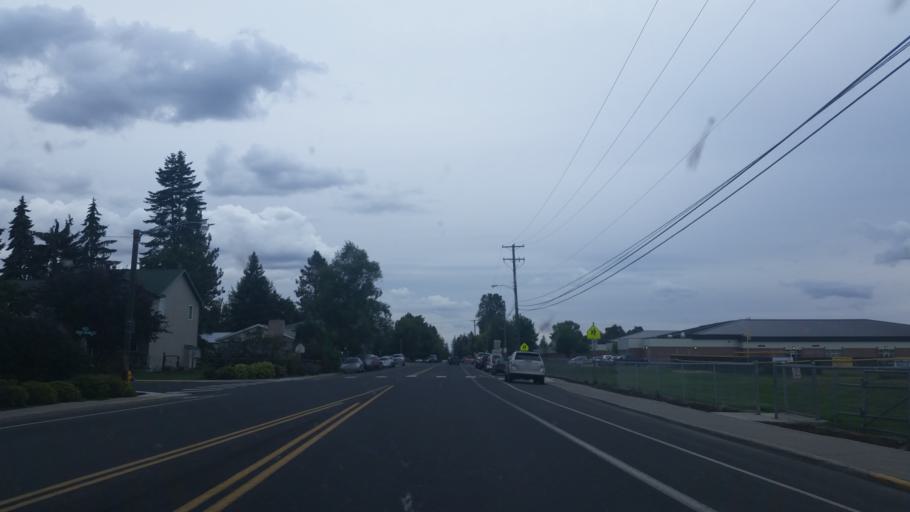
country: US
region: Washington
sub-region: Spokane County
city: Cheney
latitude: 47.5000
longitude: -117.5756
